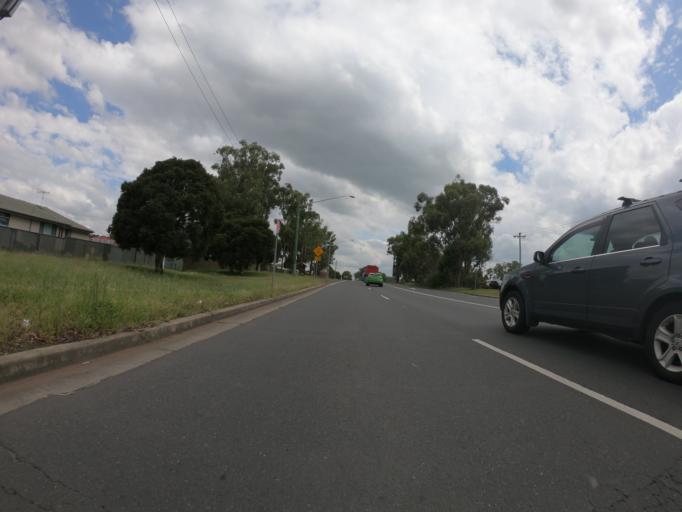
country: AU
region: New South Wales
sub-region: Blacktown
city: Mount Druitt
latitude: -33.7884
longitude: 150.7704
